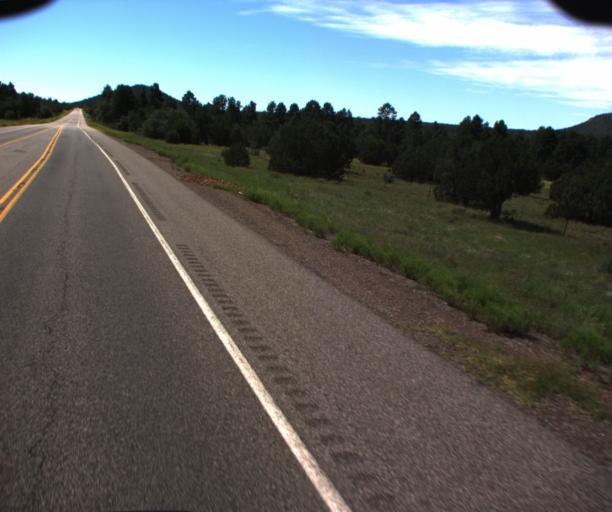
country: US
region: Arizona
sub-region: Gila County
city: San Carlos
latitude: 33.6732
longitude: -110.5727
